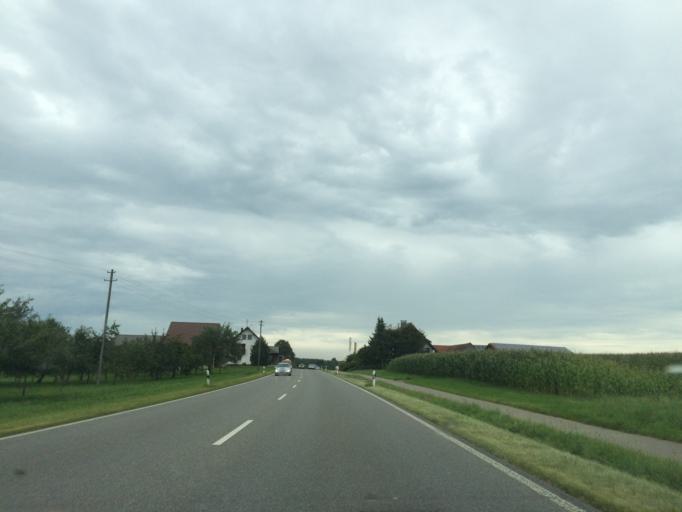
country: DE
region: Baden-Wuerttemberg
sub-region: Tuebingen Region
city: Horgenzell
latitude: 47.7499
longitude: 9.5116
